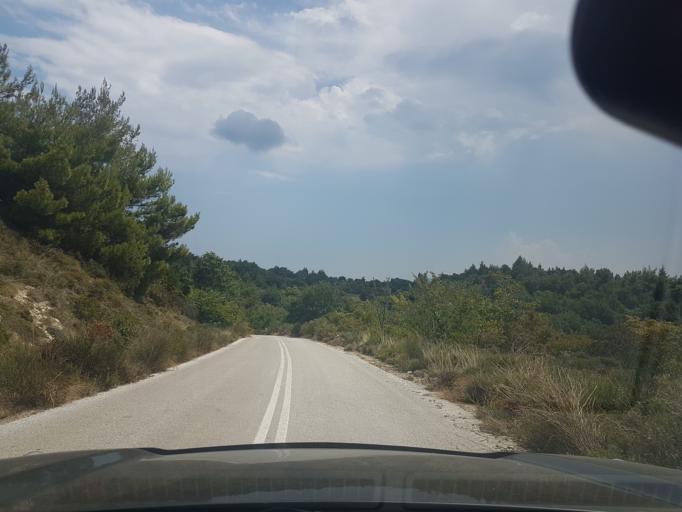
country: GR
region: Central Greece
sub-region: Nomos Evvoias
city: Kymi
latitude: 38.6474
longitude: 24.0468
